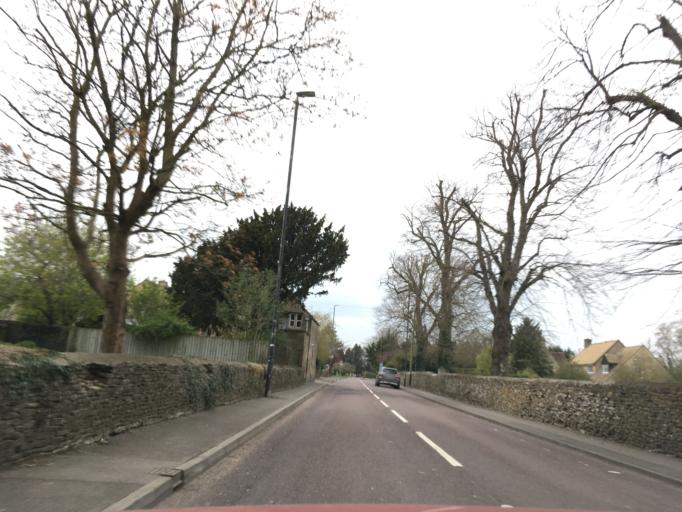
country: GB
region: England
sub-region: Gloucestershire
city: Cirencester
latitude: 51.7093
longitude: -1.9753
